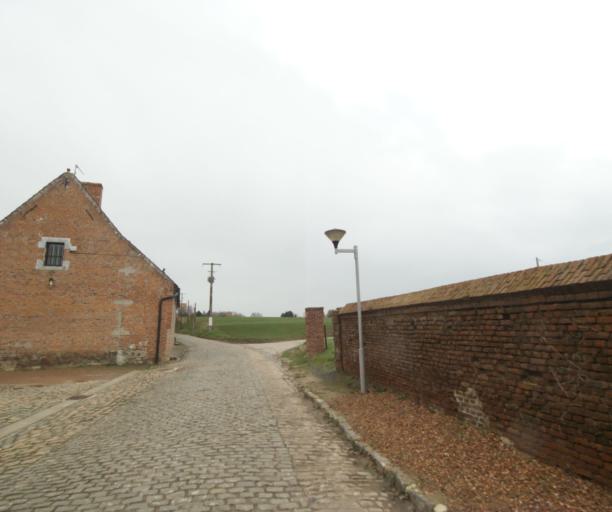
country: FR
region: Nord-Pas-de-Calais
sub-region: Departement du Nord
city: Quievrechain
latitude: 50.3789
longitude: 3.6643
